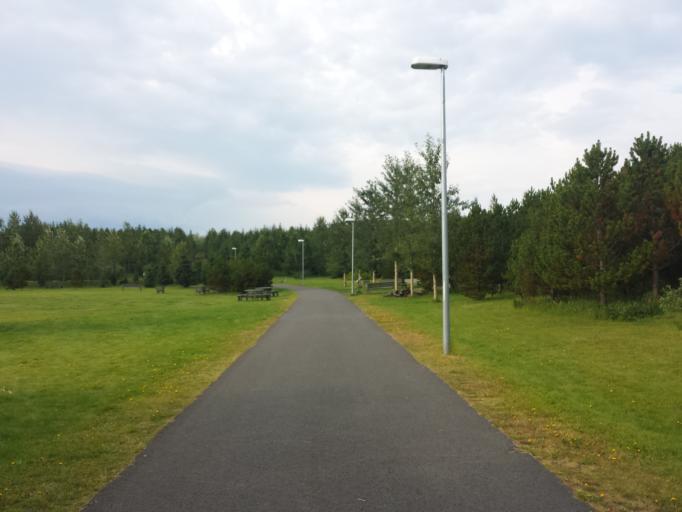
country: IS
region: Capital Region
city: Reykjavik
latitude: 64.0733
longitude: -21.8244
